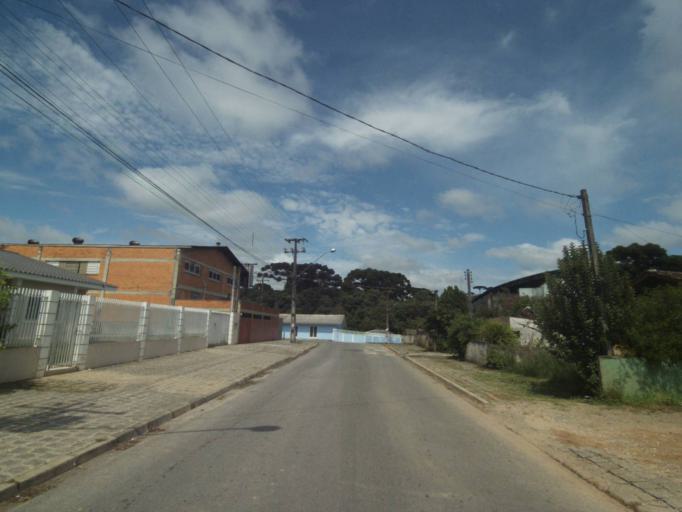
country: BR
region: Parana
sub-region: Campina Grande Do Sul
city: Campina Grande do Sul
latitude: -25.3040
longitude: -49.0537
